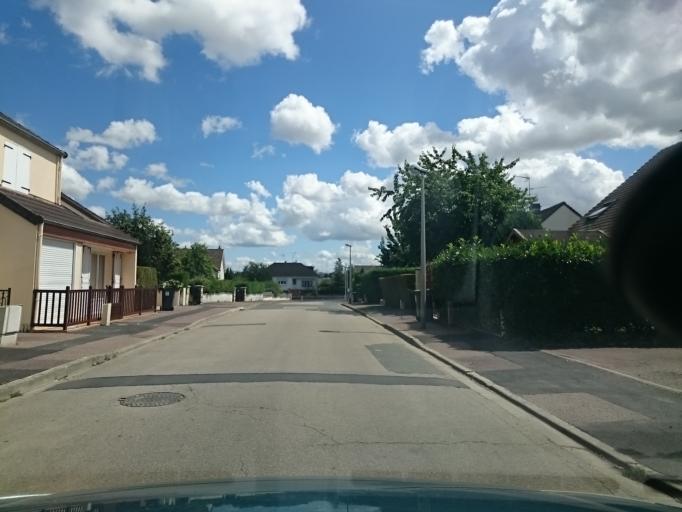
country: FR
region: Lower Normandy
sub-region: Departement du Calvados
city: Ifs
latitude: 49.1432
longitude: -0.3525
